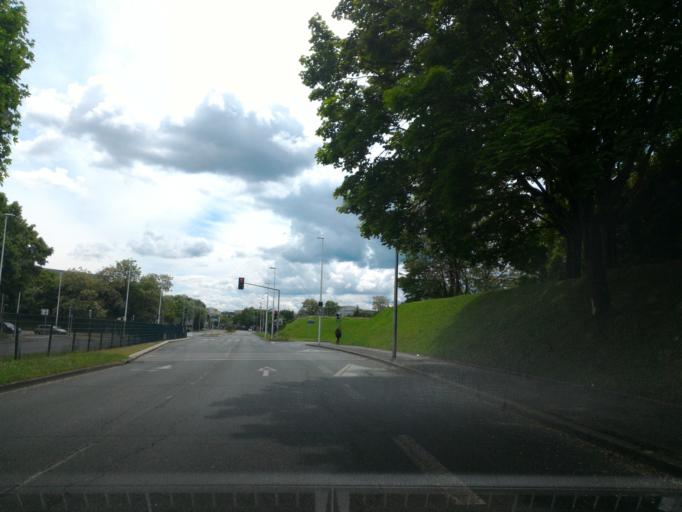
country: FR
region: Ile-de-France
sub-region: Departement de Seine-et-Marne
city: Torcy
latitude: 48.8470
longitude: 2.6453
